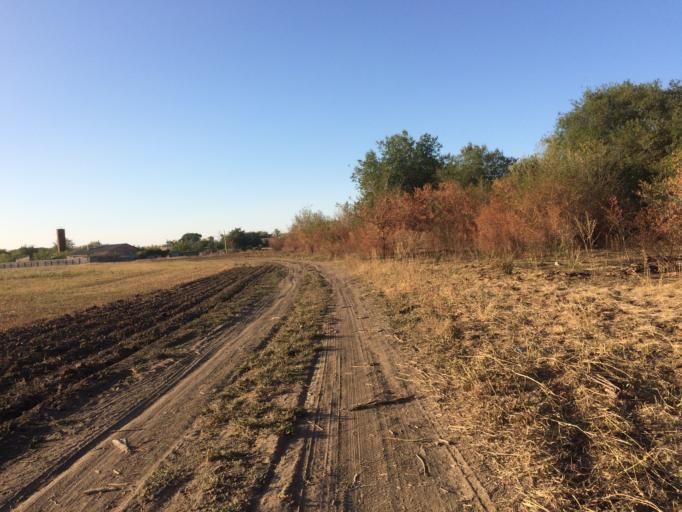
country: RU
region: Rostov
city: Gigant
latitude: 46.5116
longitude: 41.1899
